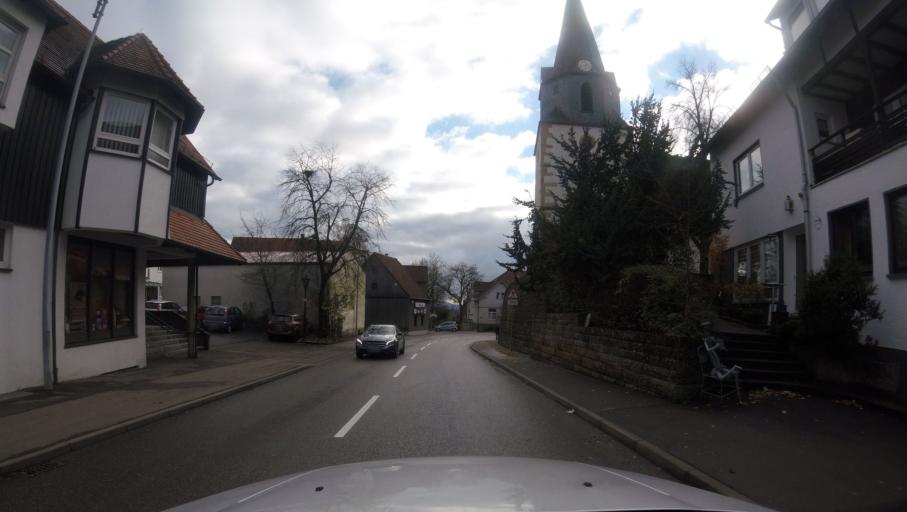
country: DE
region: Baden-Wuerttemberg
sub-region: Regierungsbezirk Stuttgart
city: Spraitbach
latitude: 48.8803
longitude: 9.7624
